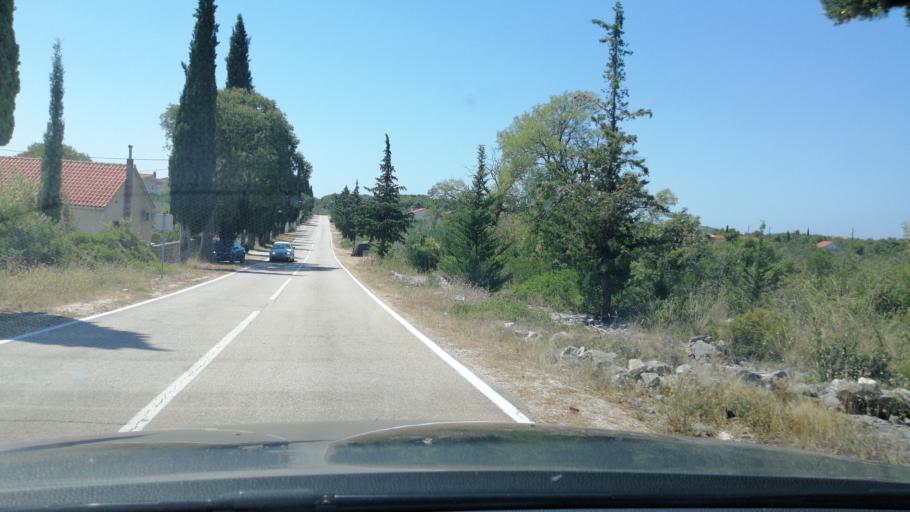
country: HR
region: Sibensko-Kniniska
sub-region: Grad Sibenik
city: Pirovac
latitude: 43.8286
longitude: 15.6798
